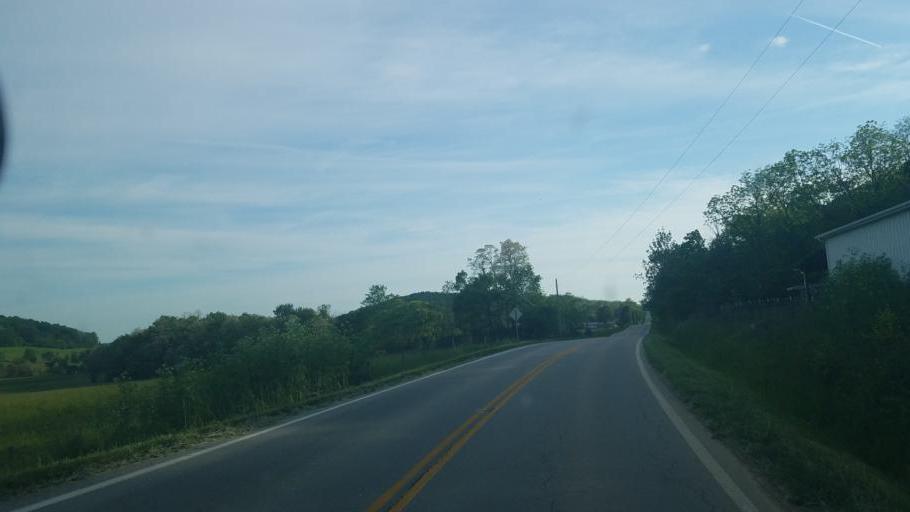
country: US
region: Ohio
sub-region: Ross County
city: Frankfort
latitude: 39.4169
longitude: -83.2706
